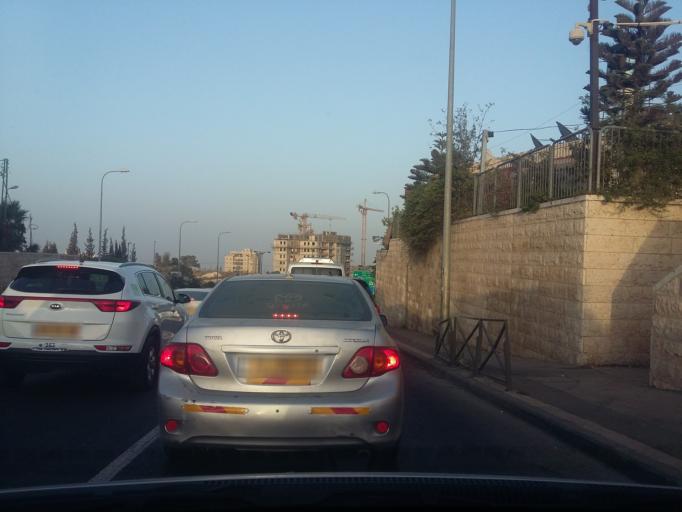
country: PS
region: West Bank
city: Ar Ram wa Dahiyat al Barid
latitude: 31.8275
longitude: 35.2345
